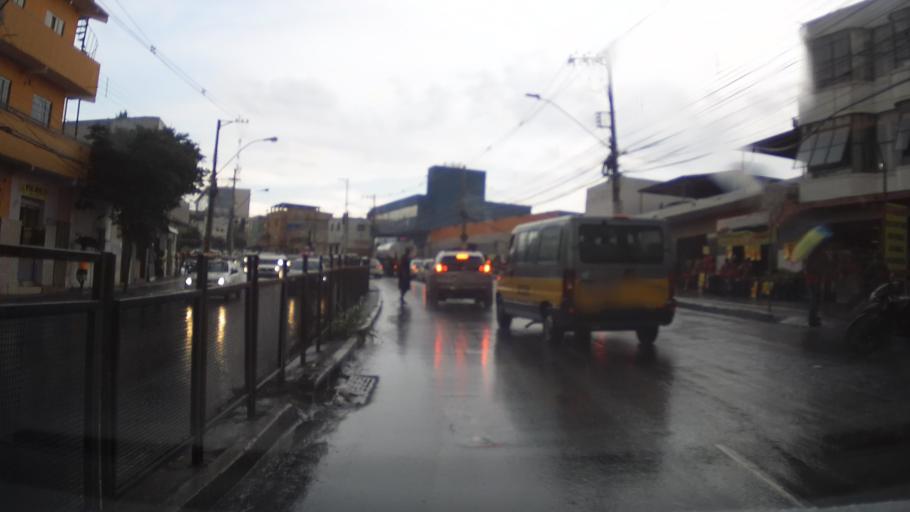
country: BR
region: Minas Gerais
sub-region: Belo Horizonte
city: Belo Horizonte
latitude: -19.9499
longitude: -43.9613
